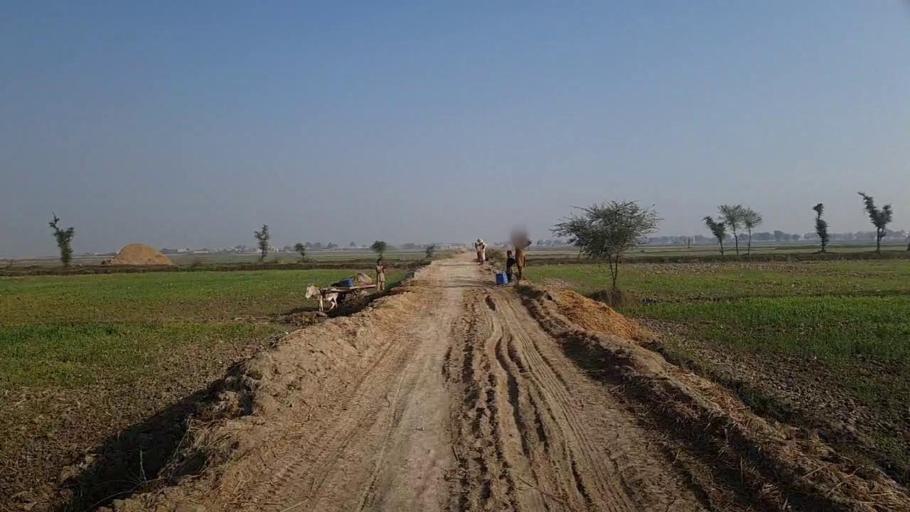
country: PK
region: Sindh
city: Sita Road
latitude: 27.1120
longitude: 67.8928
